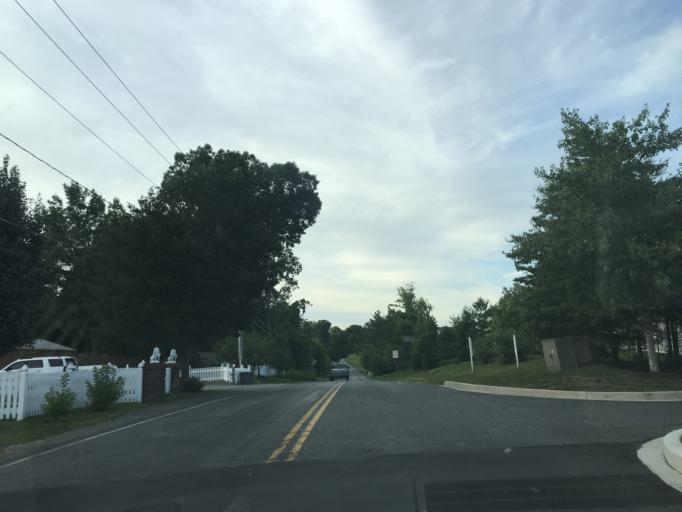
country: US
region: Maryland
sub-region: Harford County
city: Perryman
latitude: 39.4902
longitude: -76.2114
